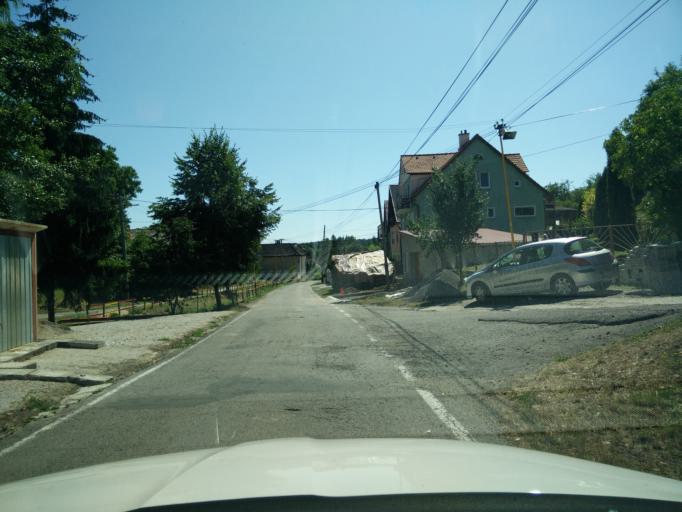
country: SK
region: Nitriansky
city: Prievidza
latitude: 48.8021
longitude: 18.7035
